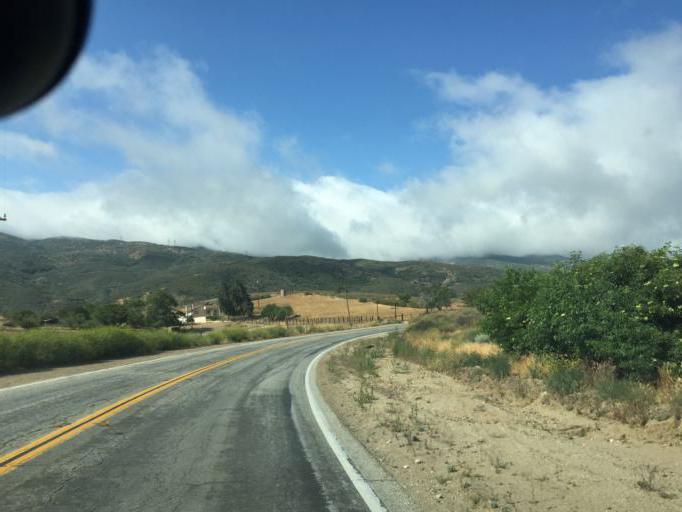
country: US
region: California
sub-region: Los Angeles County
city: Leona Valley
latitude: 34.5960
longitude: -118.2711
